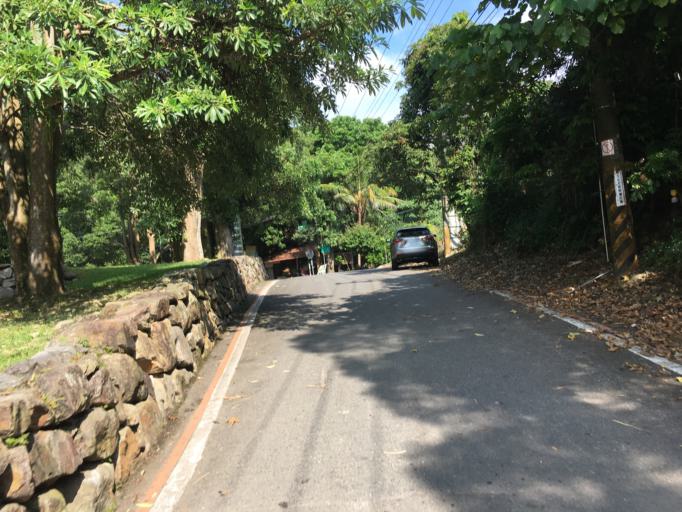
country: TW
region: Taiwan
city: Fengyuan
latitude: 24.1838
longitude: 120.7855
